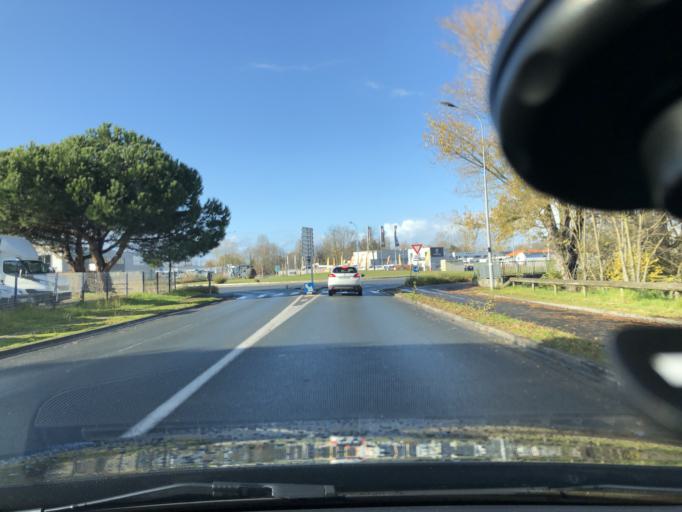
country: FR
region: Aquitaine
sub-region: Departement de la Gironde
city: Bruges
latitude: 44.8864
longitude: -0.5949
